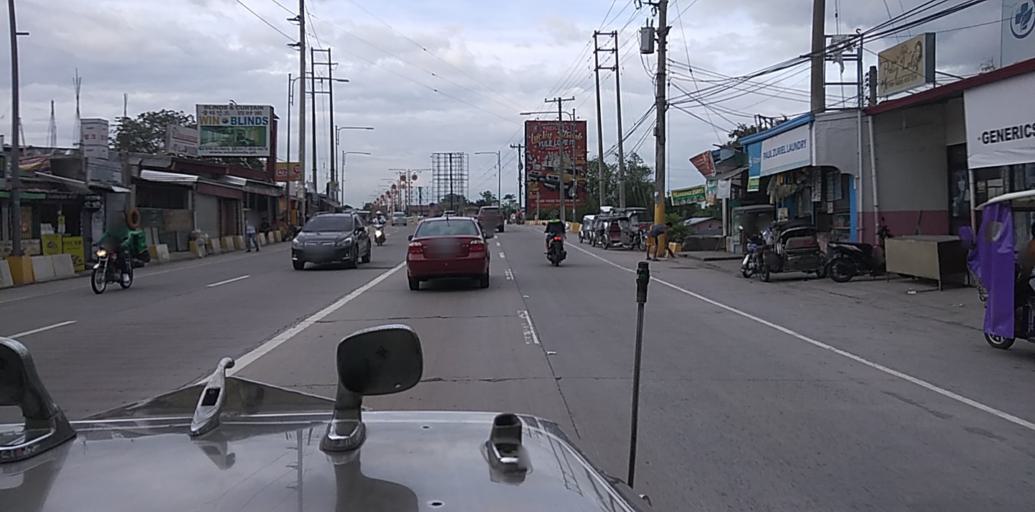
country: PH
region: Central Luzon
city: Santol
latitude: 15.1545
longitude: 120.5604
